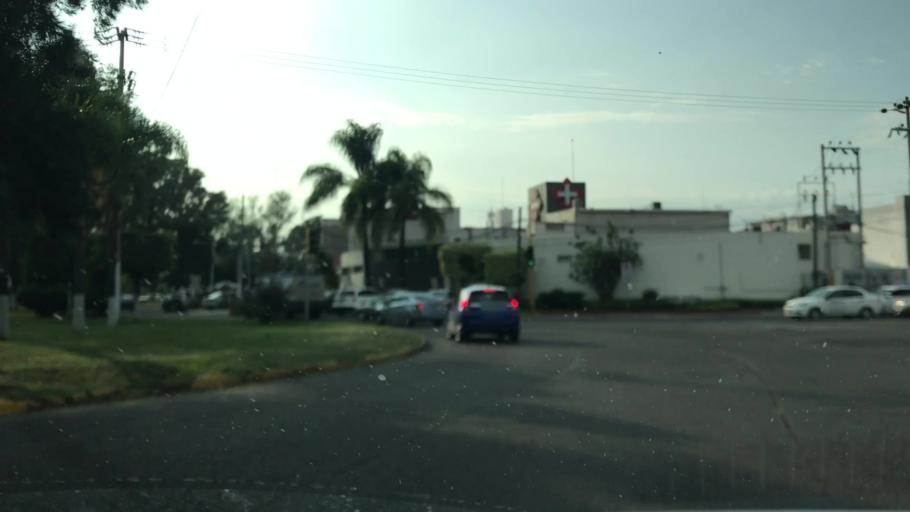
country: MX
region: Jalisco
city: Guadalajara
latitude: 20.6299
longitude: -103.4226
